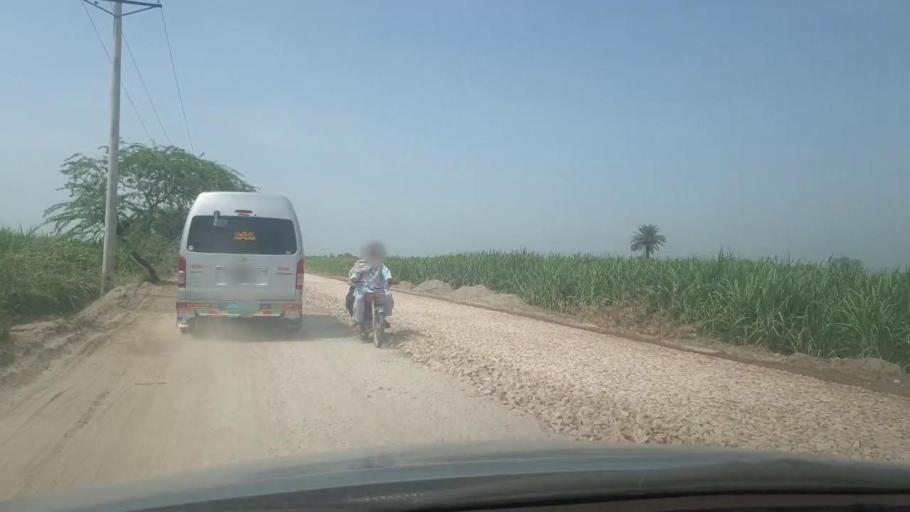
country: PK
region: Sindh
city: Ranipur
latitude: 27.2758
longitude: 68.5980
